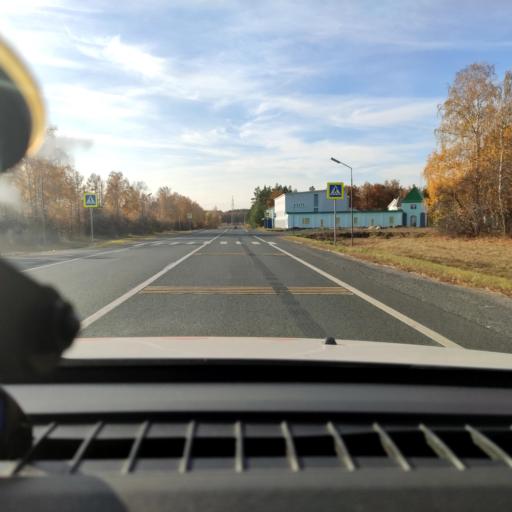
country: RU
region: Samara
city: Volzhskiy
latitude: 53.4564
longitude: 50.1265
